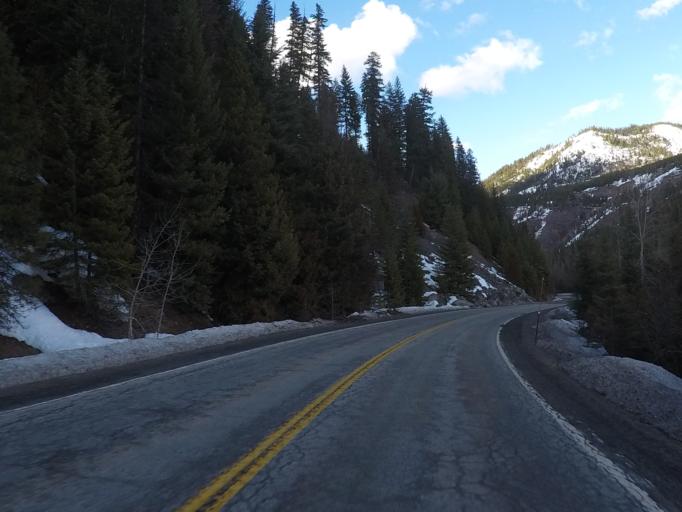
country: US
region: Montana
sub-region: Ravalli County
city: Stevensville
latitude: 46.5245
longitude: -114.6797
